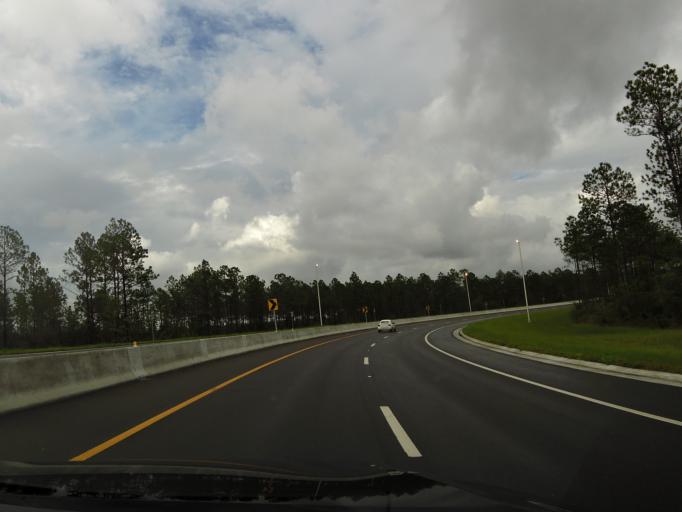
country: US
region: Florida
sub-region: Duval County
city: Baldwin
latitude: 30.3145
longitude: -81.8825
